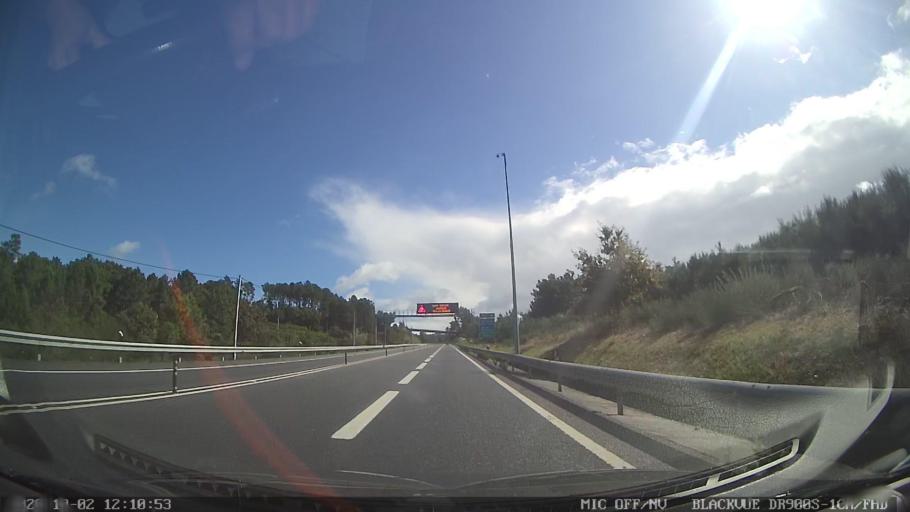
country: PT
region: Vila Real
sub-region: Vila Real
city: Vila Real
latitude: 41.3164
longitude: -7.7205
